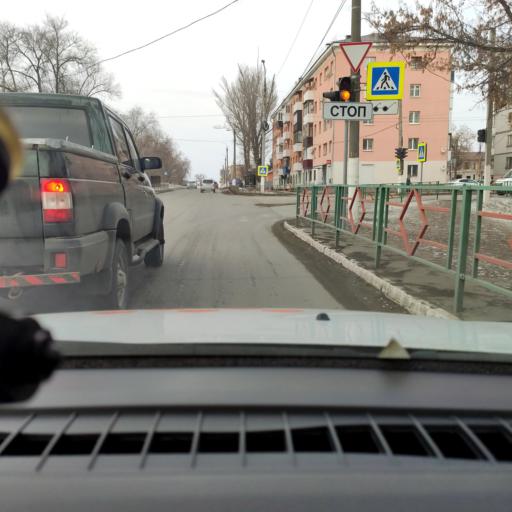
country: RU
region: Samara
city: Chapayevsk
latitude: 52.9535
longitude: 49.6862
